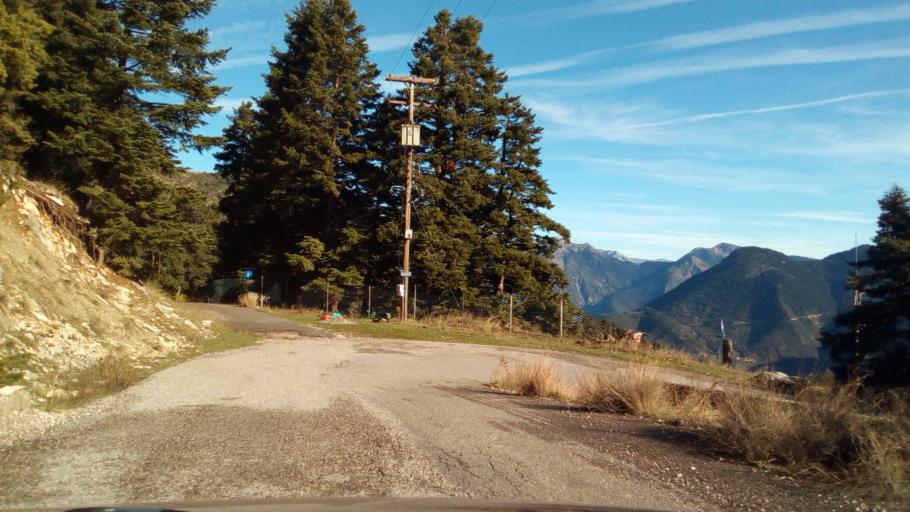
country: GR
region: West Greece
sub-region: Nomos Aitolias kai Akarnanias
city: Nafpaktos
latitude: 38.5360
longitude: 21.8406
